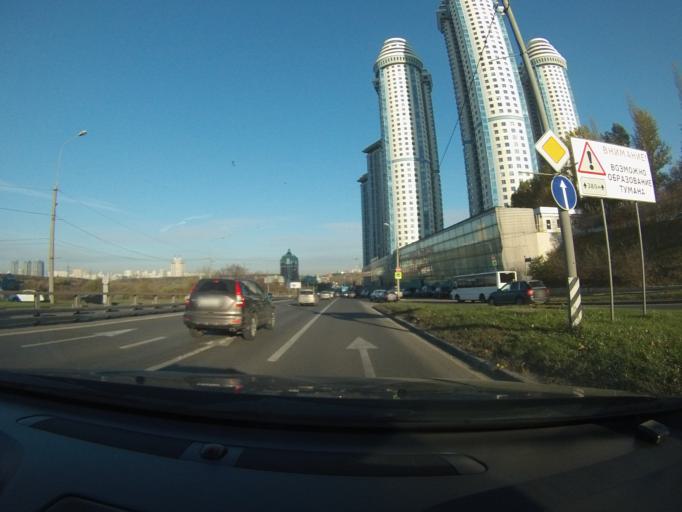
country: RU
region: Moskovskaya
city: Kastanayevo
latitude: 55.7128
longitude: 37.5049
